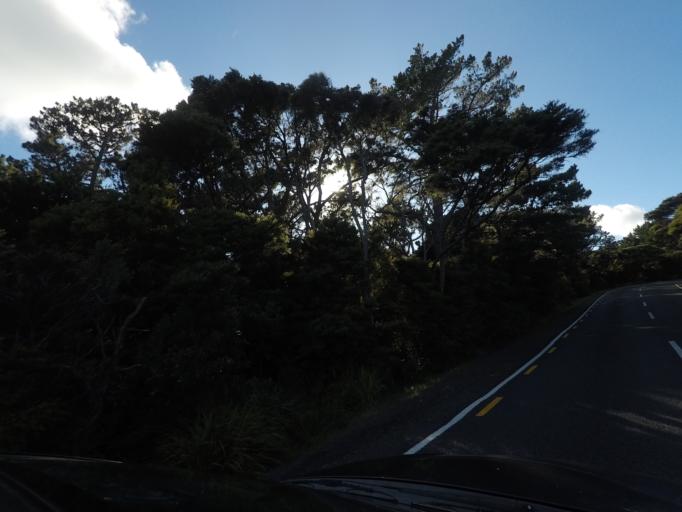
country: NZ
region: Auckland
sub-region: Auckland
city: Titirangi
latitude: -37.0062
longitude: 174.6009
